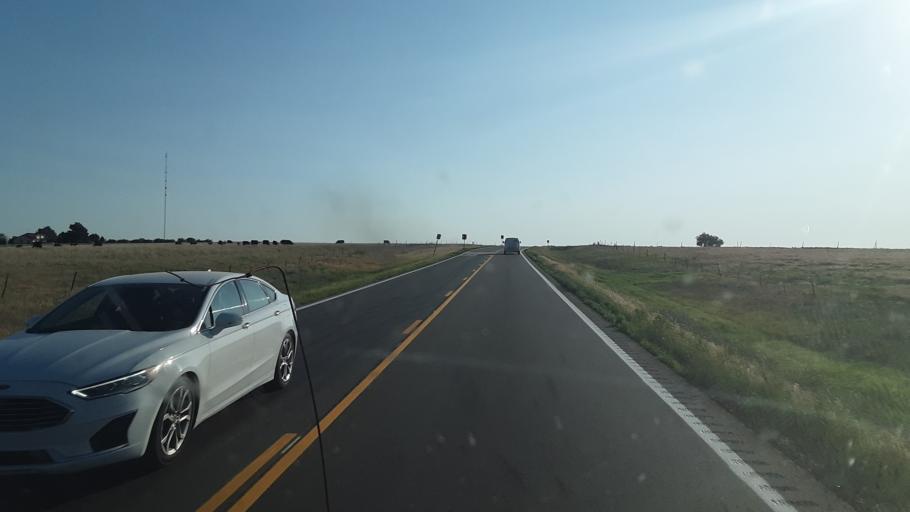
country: US
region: Kansas
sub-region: Hodgeman County
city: Jetmore
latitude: 38.0851
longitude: -99.9771
